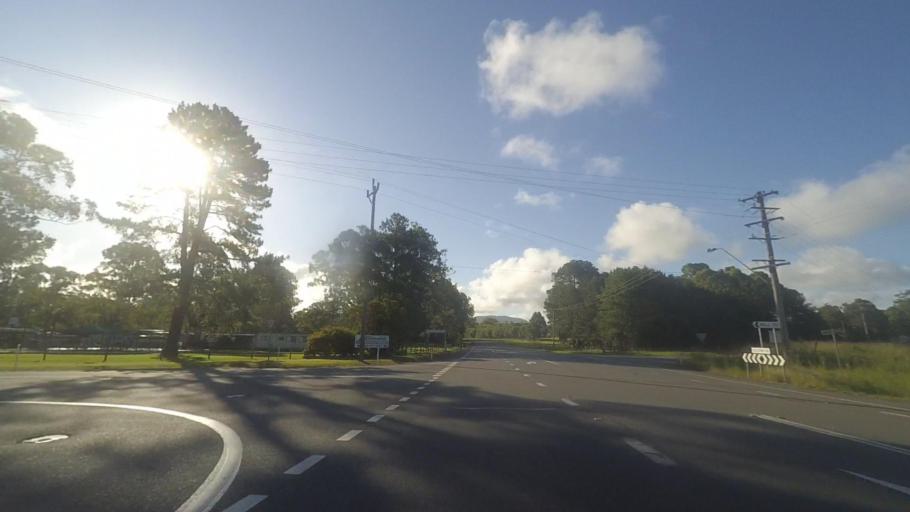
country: AU
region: New South Wales
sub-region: Great Lakes
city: Nabiac
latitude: -32.0922
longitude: 152.4478
